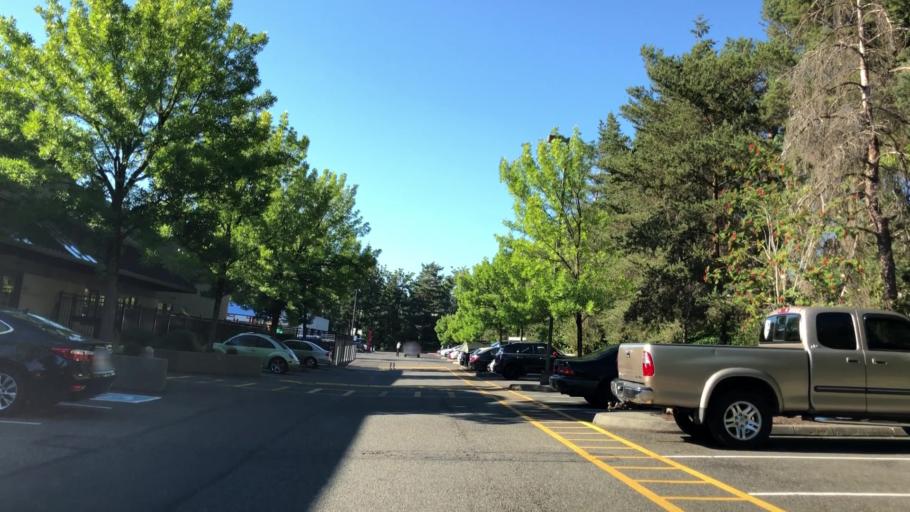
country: US
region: Washington
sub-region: King County
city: Redmond
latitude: 47.6283
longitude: -122.1473
